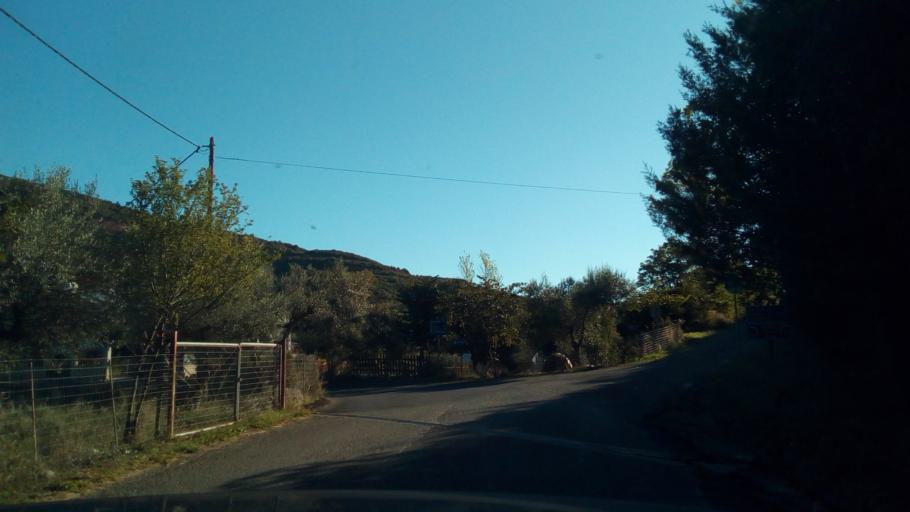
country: GR
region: West Greece
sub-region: Nomos Aitolias kai Akarnanias
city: Nafpaktos
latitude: 38.4193
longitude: 21.8435
